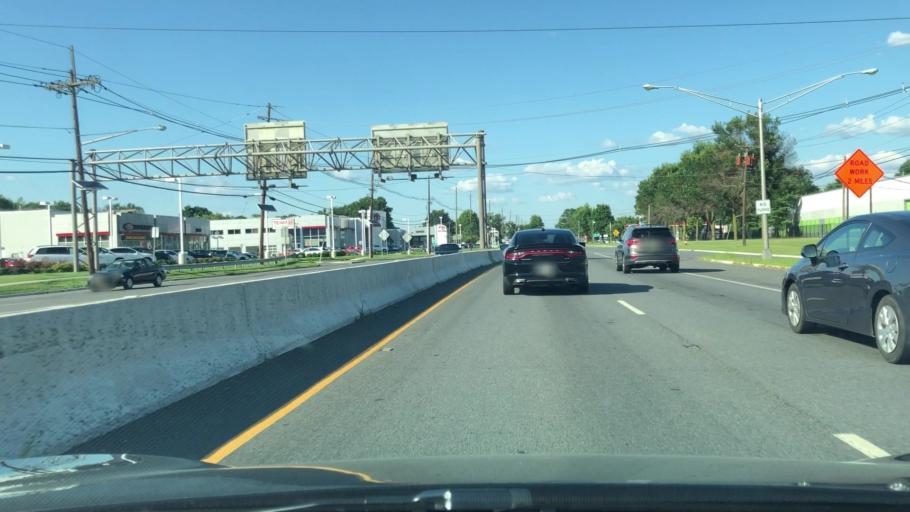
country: US
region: New Jersey
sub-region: Mercer County
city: Lawrenceville
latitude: 40.2693
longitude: -74.7131
